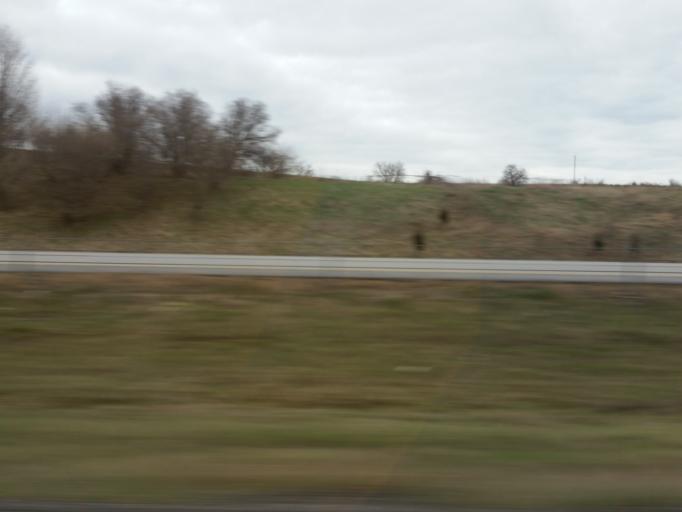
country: US
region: Iowa
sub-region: Johnson County
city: Tiffin
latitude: 41.7075
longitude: -91.6422
